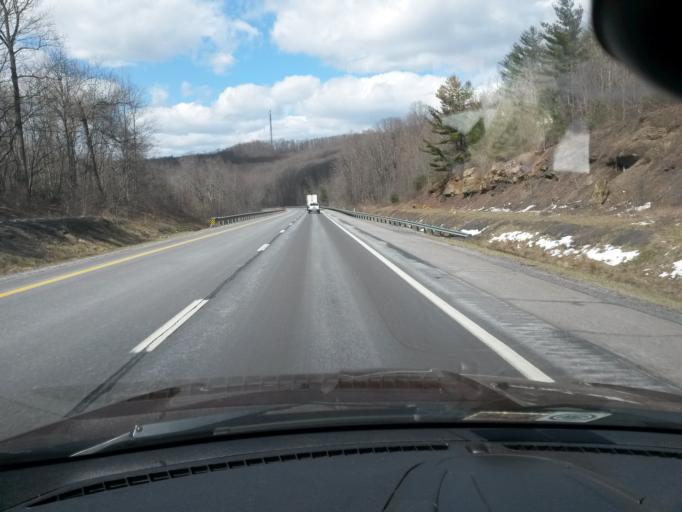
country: US
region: West Virginia
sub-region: Raleigh County
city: Shady Spring
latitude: 37.6915
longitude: -81.1291
